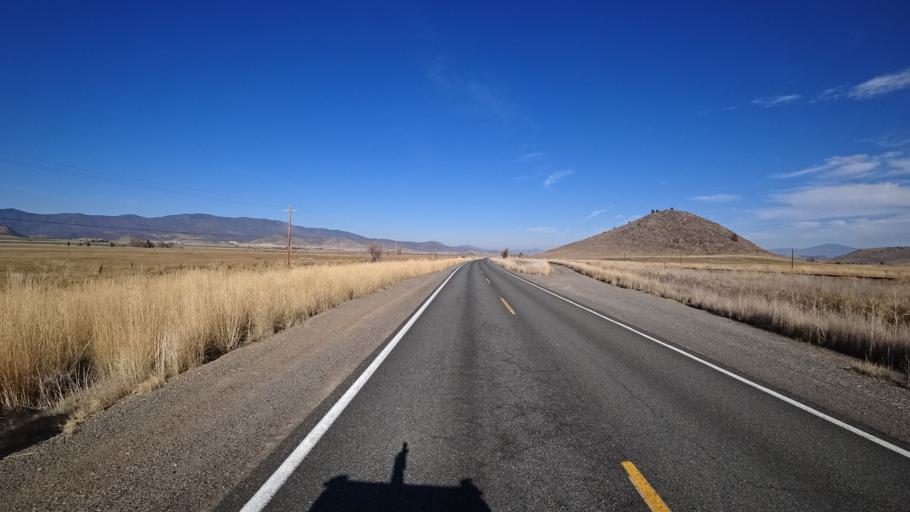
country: US
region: California
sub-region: Siskiyou County
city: Weed
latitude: 41.5295
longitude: -122.5231
